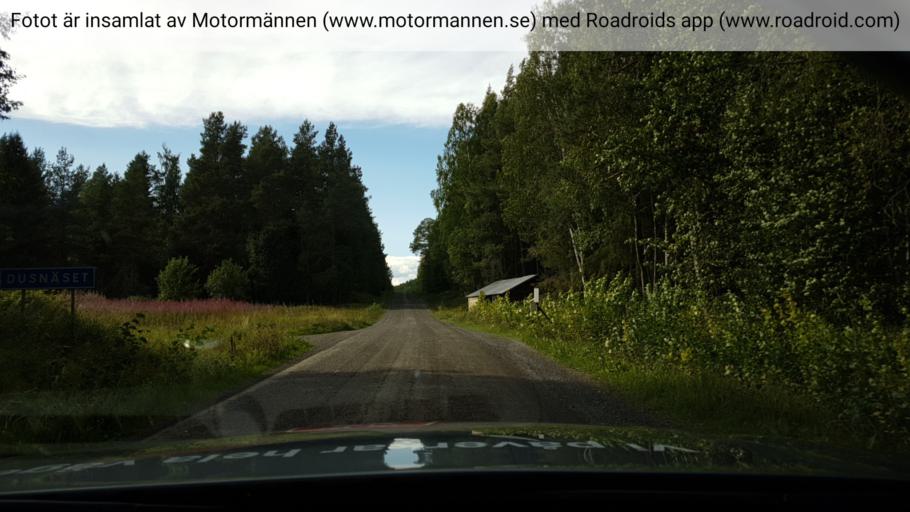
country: SE
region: Jaemtland
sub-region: Braecke Kommun
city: Braecke
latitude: 63.2073
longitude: 15.4017
